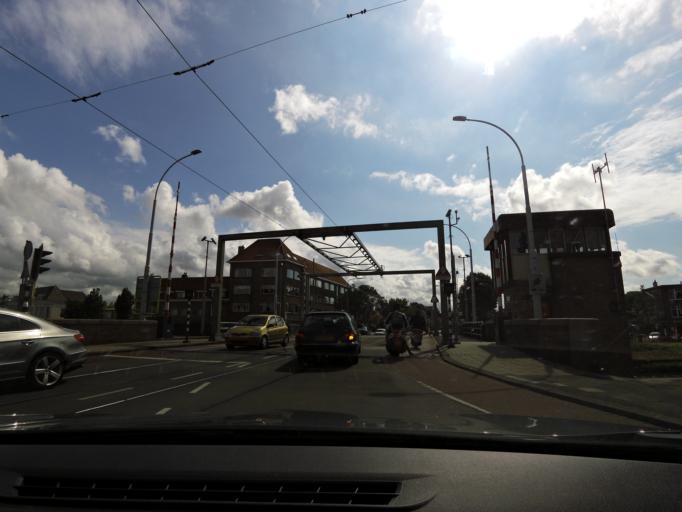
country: NL
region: South Holland
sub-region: Gemeente Leidschendam-Voorburg
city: Voorburg
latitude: 52.0597
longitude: 4.3445
